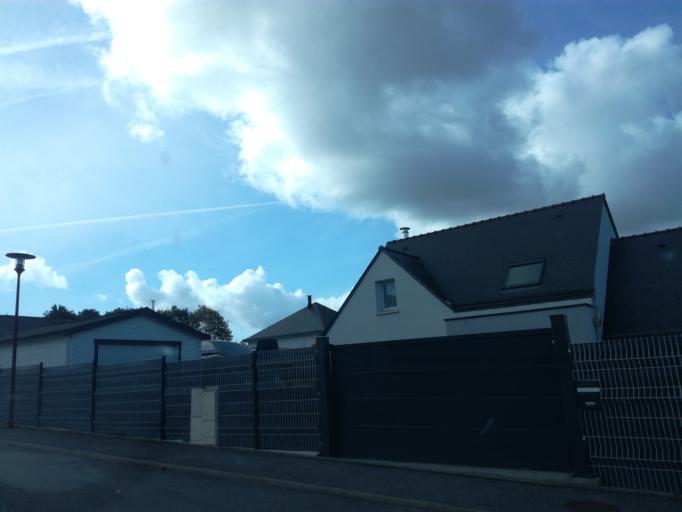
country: FR
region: Brittany
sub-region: Departement du Morbihan
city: Le Sourn
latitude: 48.0438
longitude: -2.9831
